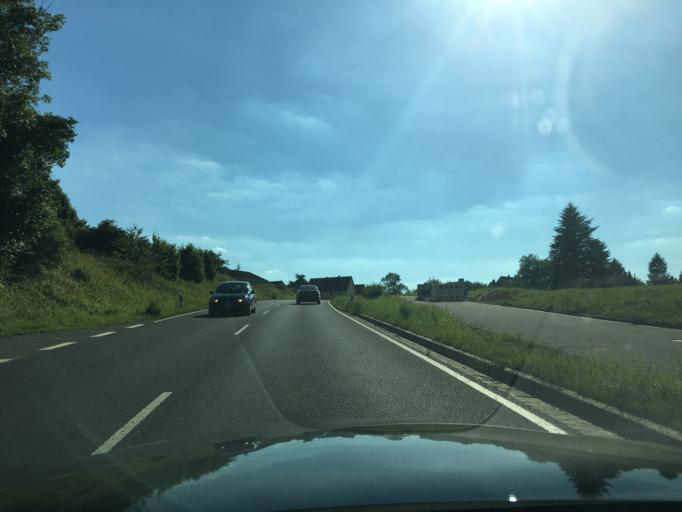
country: DE
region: Bavaria
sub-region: Upper Franconia
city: Hiltpoltstein
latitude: 49.6560
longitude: 11.2876
